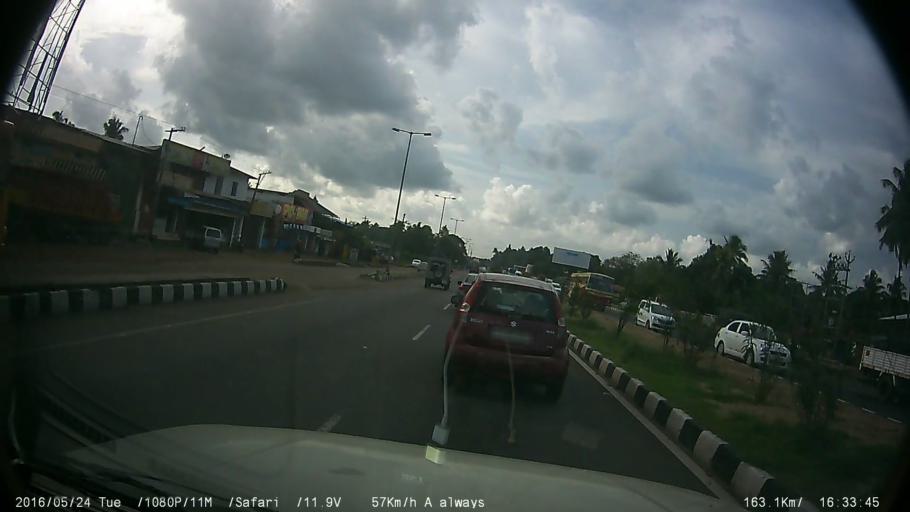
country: IN
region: Kerala
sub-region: Ernakulam
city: Angamali
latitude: 10.2501
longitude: 76.3692
